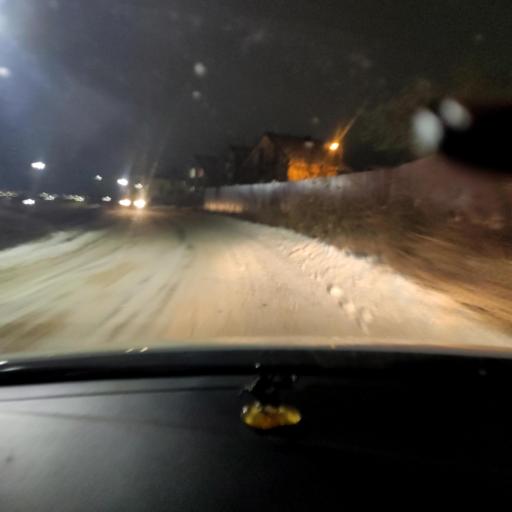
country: RU
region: Tatarstan
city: Vysokaya Gora
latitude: 55.8970
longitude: 49.3046
